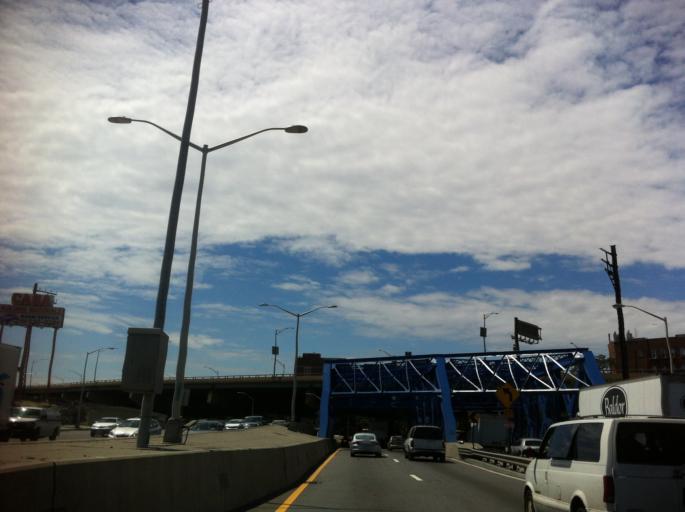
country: US
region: New York
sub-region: Bronx
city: The Bronx
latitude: 40.8227
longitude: -73.8859
